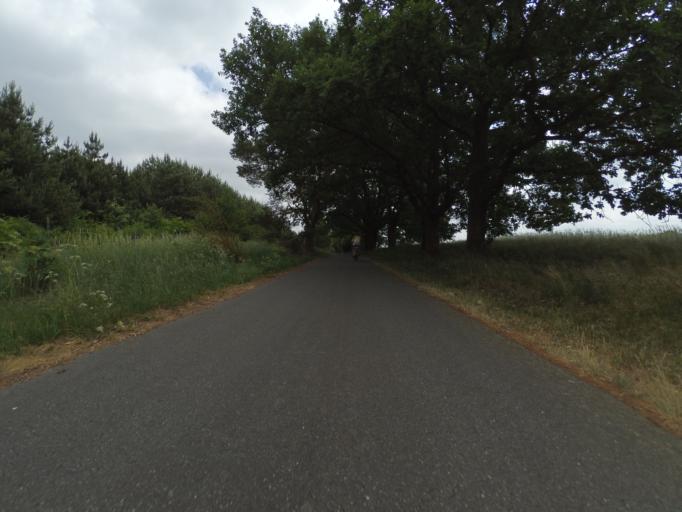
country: DE
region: Mecklenburg-Vorpommern
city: Grabowhofe
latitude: 53.5319
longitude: 12.5637
